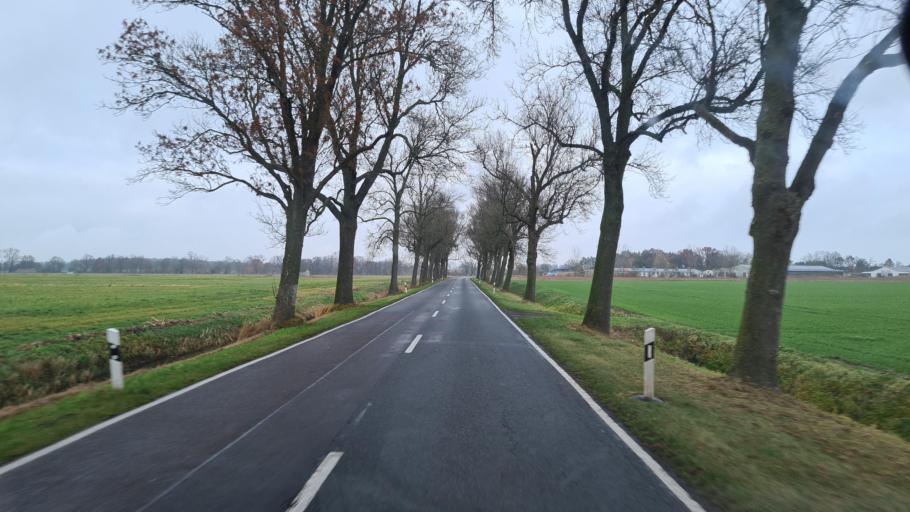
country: DE
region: Brandenburg
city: Retzow
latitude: 52.5996
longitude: 12.6448
